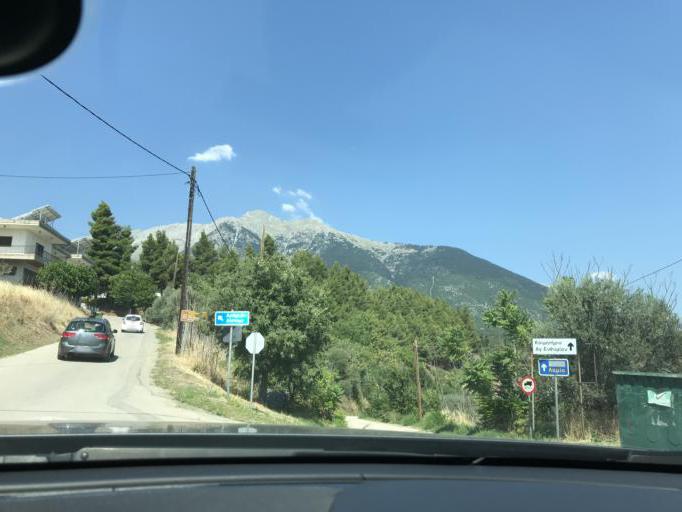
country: GR
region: Central Greece
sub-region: Nomos Fthiotidos
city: Kato Tithorea
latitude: 38.5169
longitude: 22.7343
